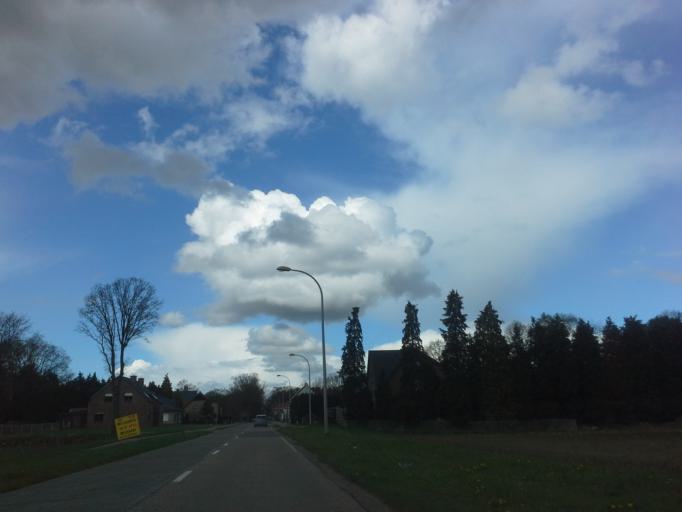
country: BE
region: Flanders
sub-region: Provincie Antwerpen
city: Meerhout
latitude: 51.1373
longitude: 5.0628
